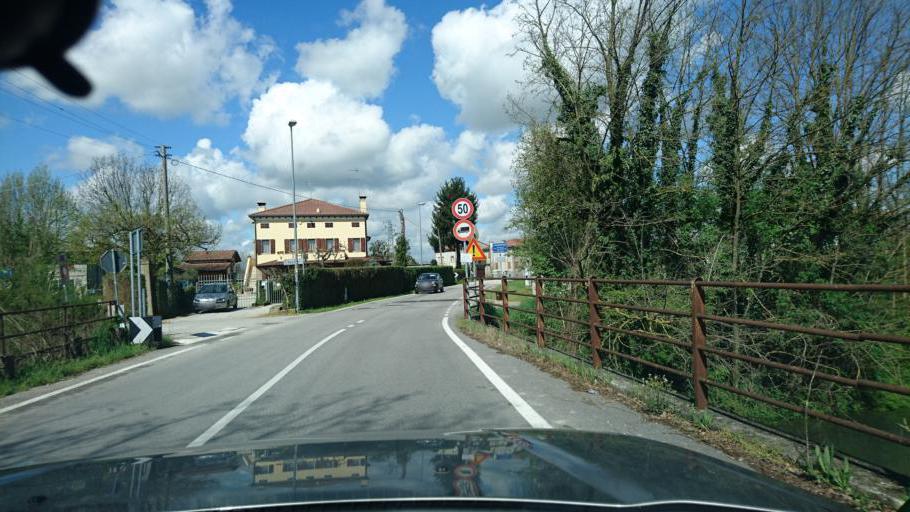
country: IT
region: Veneto
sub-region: Provincia di Padova
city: Tavo
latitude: 45.5006
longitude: 11.8524
